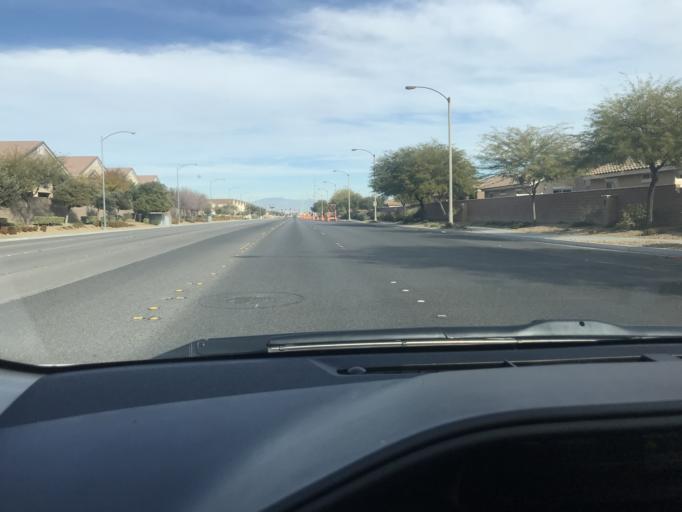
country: US
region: Nevada
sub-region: Clark County
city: Enterprise
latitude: 36.0158
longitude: -115.2796
